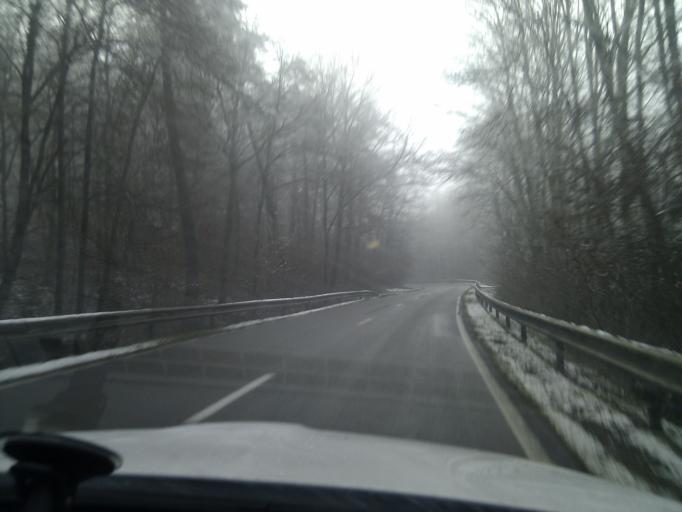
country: BE
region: Wallonia
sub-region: Province du Luxembourg
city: Libin
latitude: 49.9803
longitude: 5.1829
